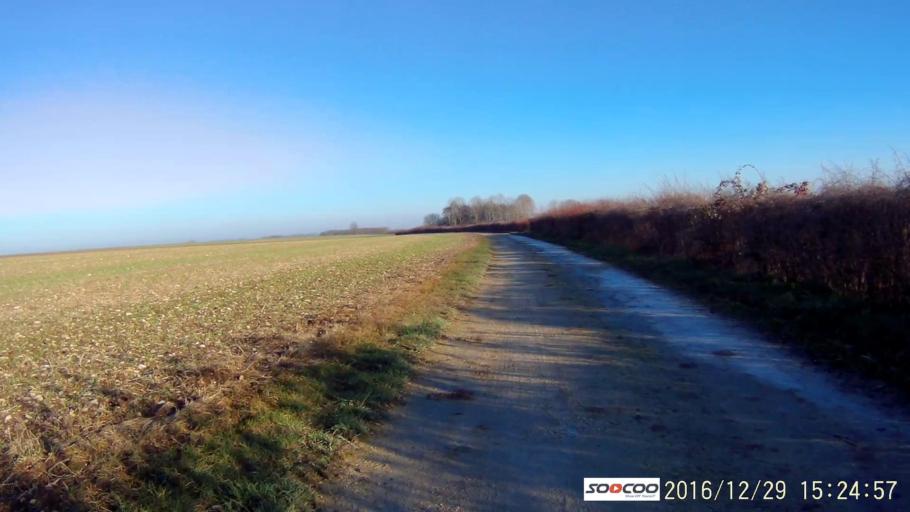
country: FR
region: Centre
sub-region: Departement de l'Indre
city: Neuvy-Pailloux
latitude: 46.9367
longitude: 1.8212
